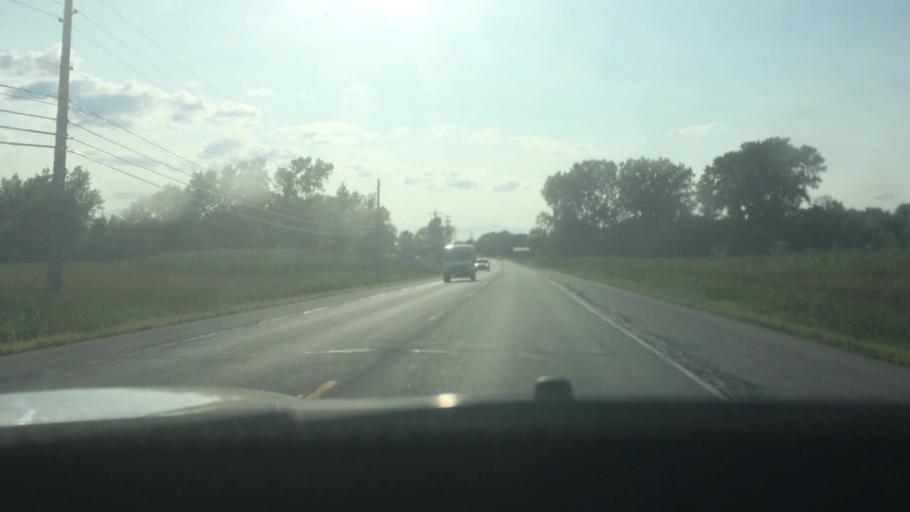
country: US
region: New York
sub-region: St. Lawrence County
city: Potsdam
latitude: 44.6674
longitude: -75.0157
